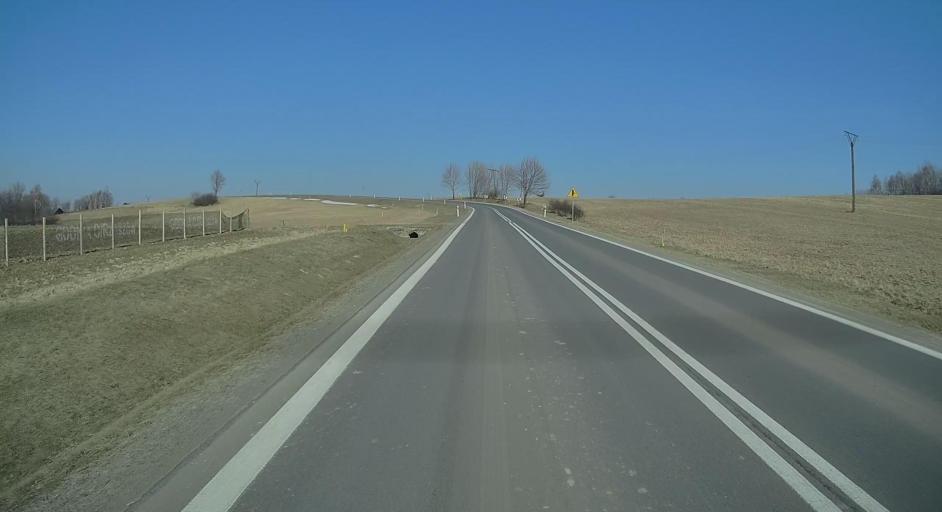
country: PL
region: Subcarpathian Voivodeship
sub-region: Powiat sanocki
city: Tyrawa Woloska
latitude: 49.6258
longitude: 22.4287
